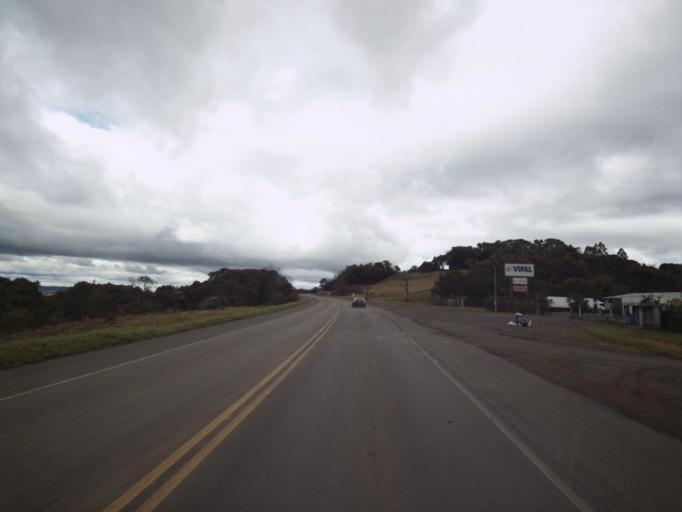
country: BR
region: Santa Catarina
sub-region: Concordia
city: Concordia
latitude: -27.2570
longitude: -51.9545
